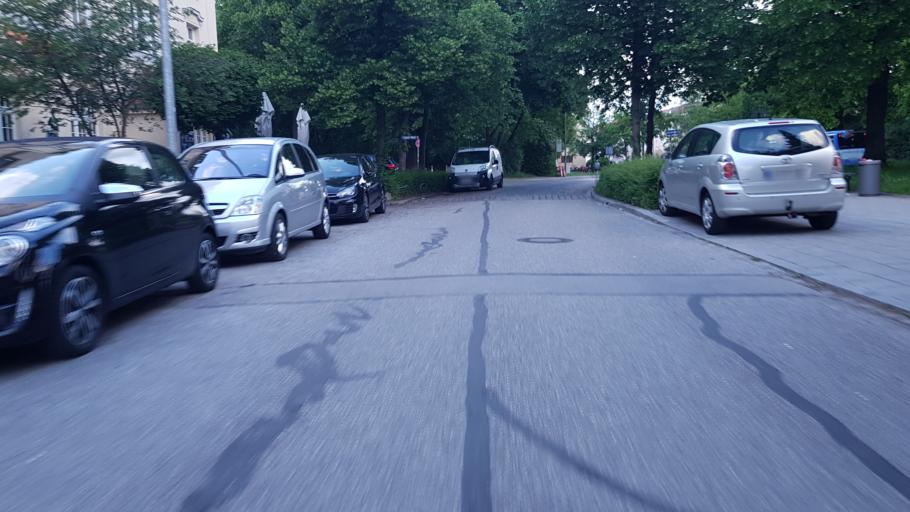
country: DE
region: Bavaria
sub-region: Upper Bavaria
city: Pasing
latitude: 48.1345
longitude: 11.4992
